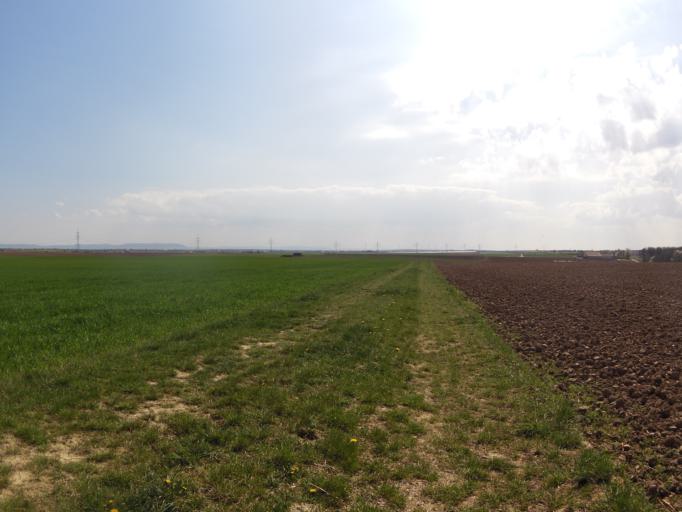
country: DE
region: Bavaria
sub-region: Regierungsbezirk Unterfranken
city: Oberpleichfeld
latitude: 49.8506
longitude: 10.0752
